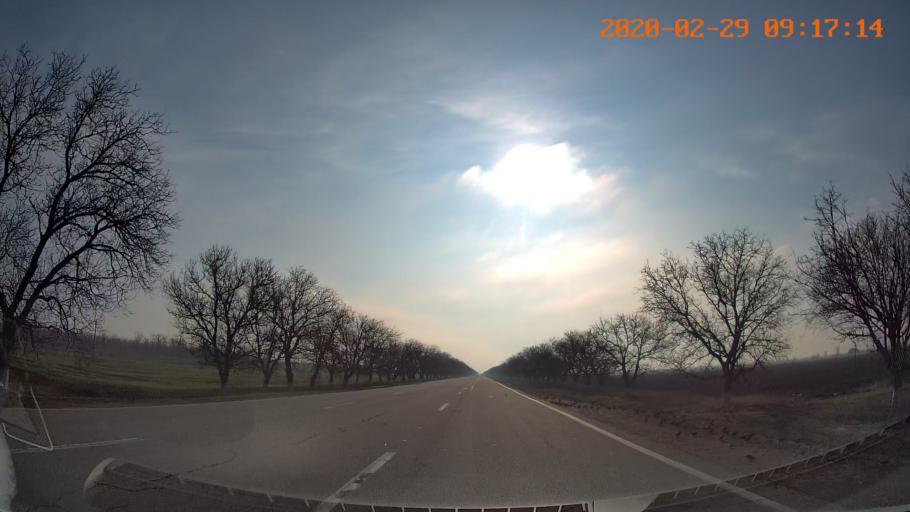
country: MD
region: Telenesti
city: Pervomaisc
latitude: 46.7848
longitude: 29.9006
